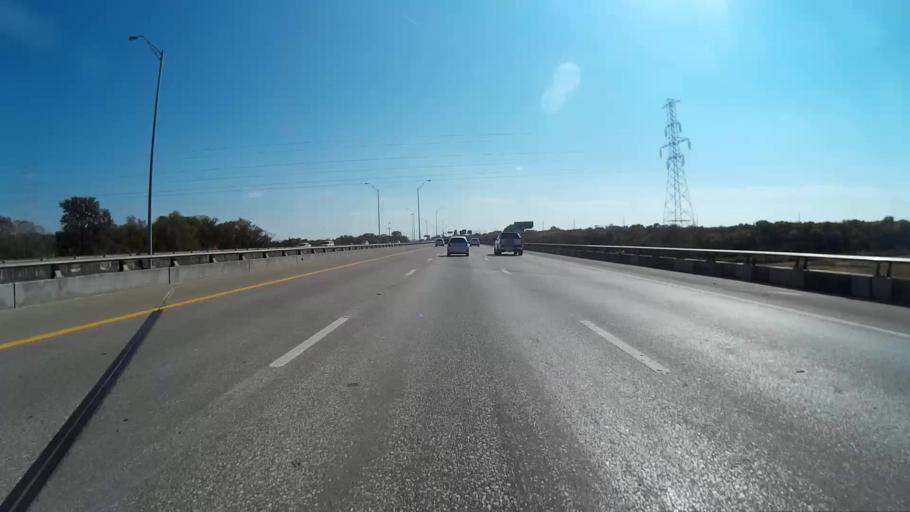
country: US
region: Texas
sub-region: Dallas County
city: Dallas
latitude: 32.7306
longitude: -96.7642
